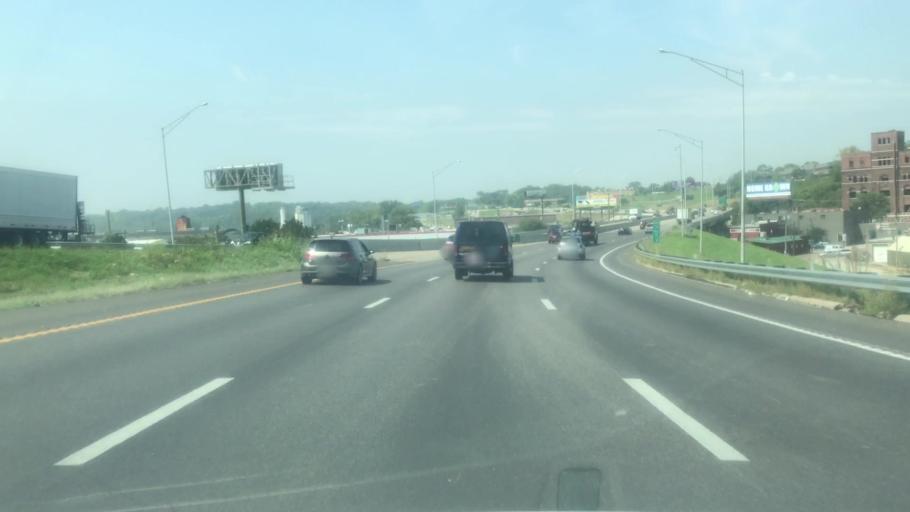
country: US
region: Missouri
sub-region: Jackson County
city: Kansas City
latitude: 39.0758
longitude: -94.5994
